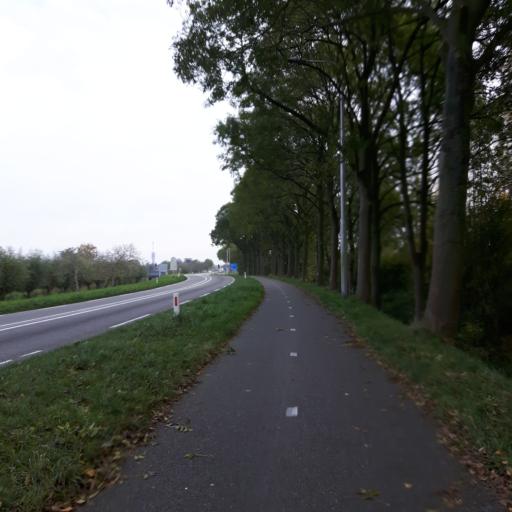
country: NL
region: Zeeland
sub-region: Gemeente Goes
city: Goes
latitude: 51.5024
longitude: 3.8541
